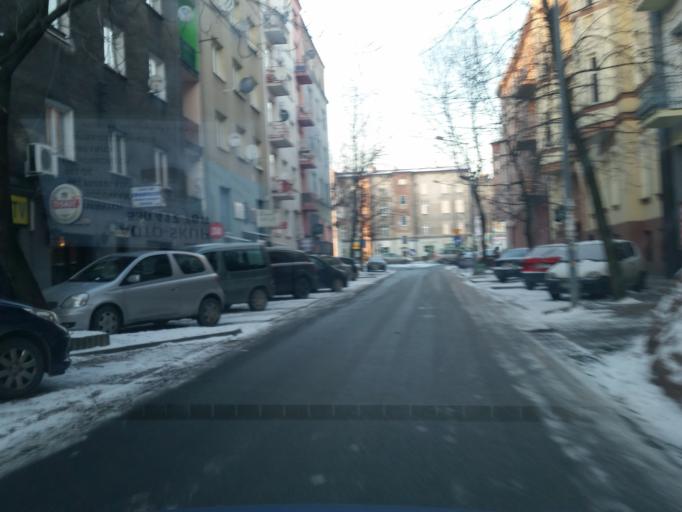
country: PL
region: Silesian Voivodeship
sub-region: Sosnowiec
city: Sosnowiec
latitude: 50.2734
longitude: 19.1284
